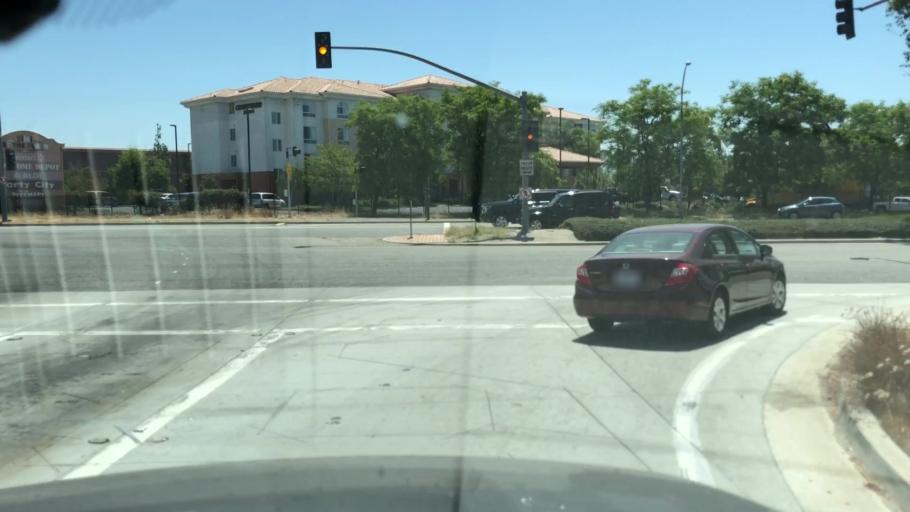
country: US
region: California
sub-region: Ventura County
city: Simi Valley
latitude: 34.2829
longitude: -118.7940
